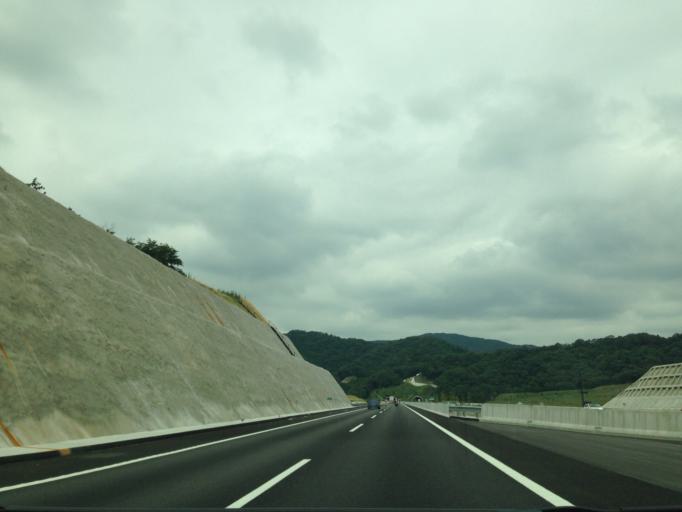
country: JP
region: Aichi
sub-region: Tokai-shi
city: Toyokawa
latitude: 34.8896
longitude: 137.3508
